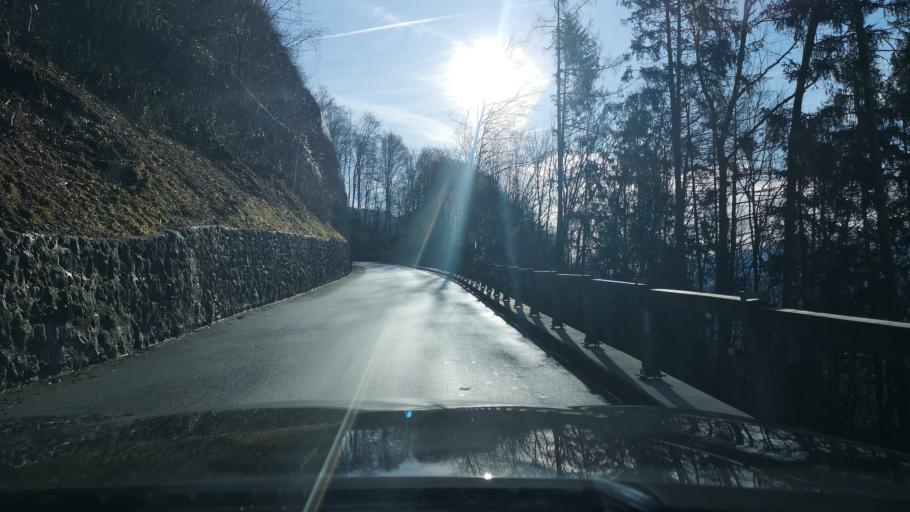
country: LI
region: Vaduz
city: Vaduz
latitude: 47.1316
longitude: 9.5301
